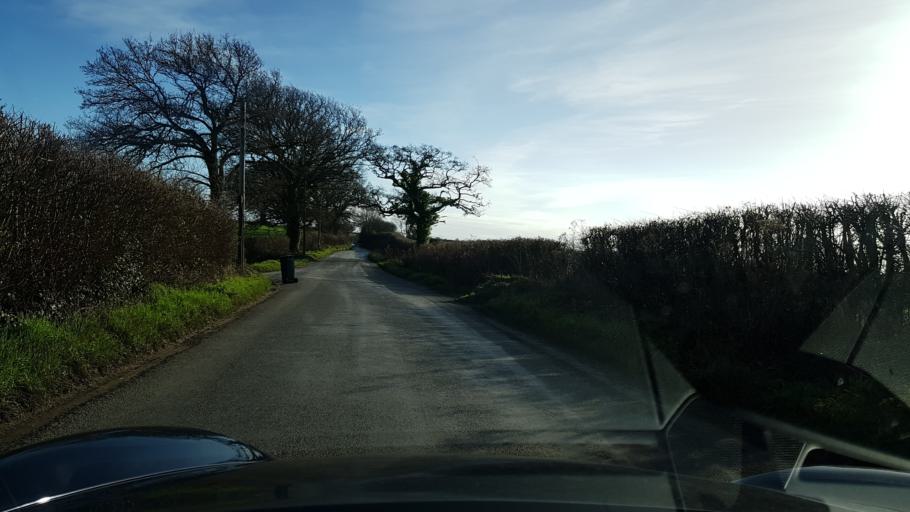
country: GB
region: England
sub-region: Dorset
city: Bridport
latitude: 50.7608
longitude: -2.7911
